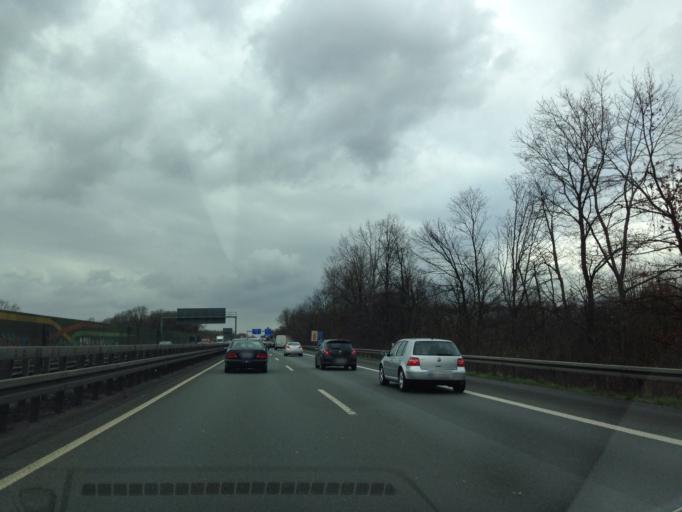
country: DE
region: North Rhine-Westphalia
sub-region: Regierungsbezirk Munster
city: Recklinghausen
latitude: 51.5741
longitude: 7.1923
